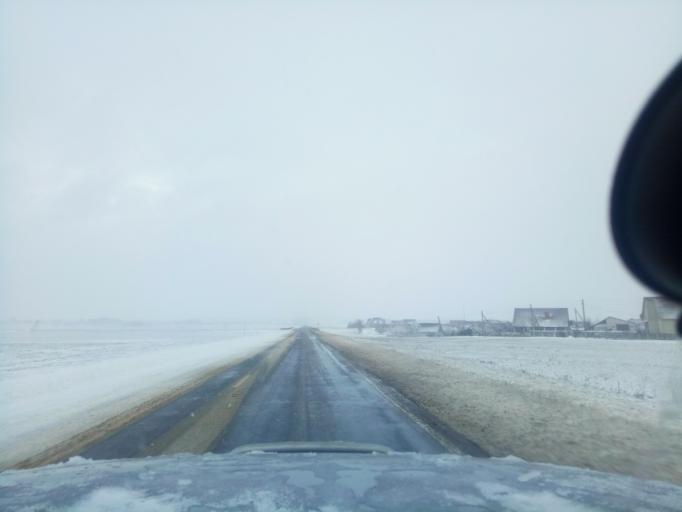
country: BY
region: Minsk
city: Haradzyeya
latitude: 53.3107
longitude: 26.5672
